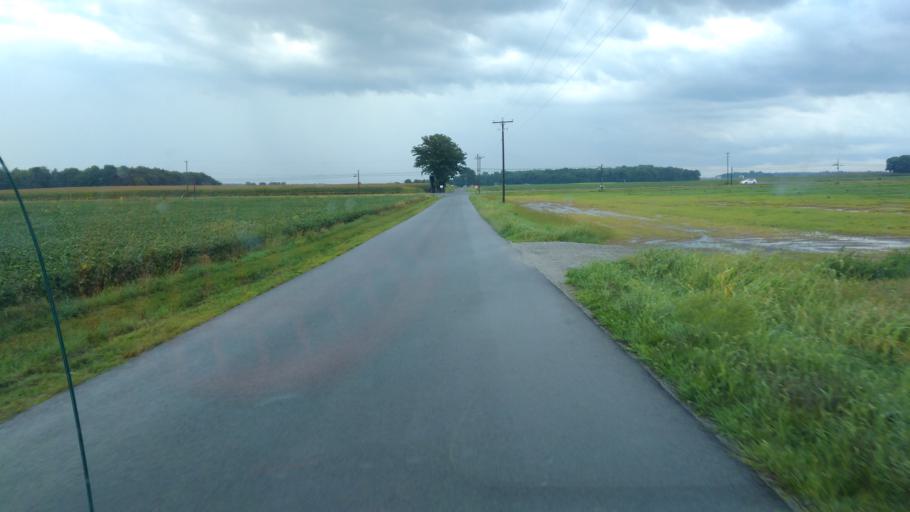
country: US
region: Ohio
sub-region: Hardin County
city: Kenton
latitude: 40.6892
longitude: -83.6186
